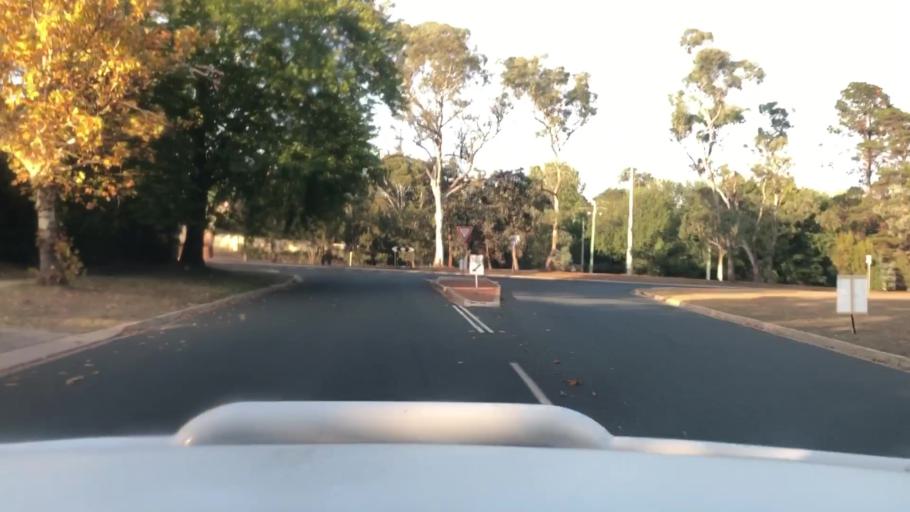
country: AU
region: Australian Capital Territory
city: Canberra
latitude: -35.2529
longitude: 149.1604
